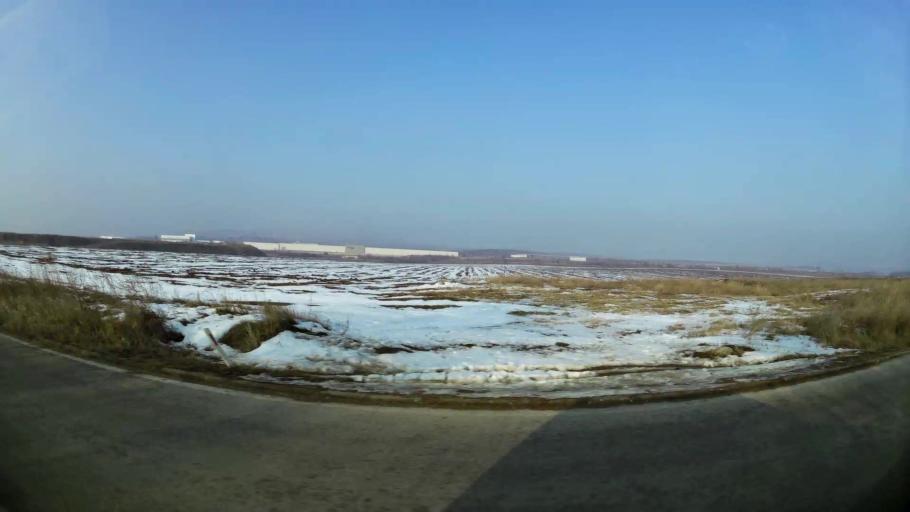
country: MK
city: Miladinovci
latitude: 41.9771
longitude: 21.6279
